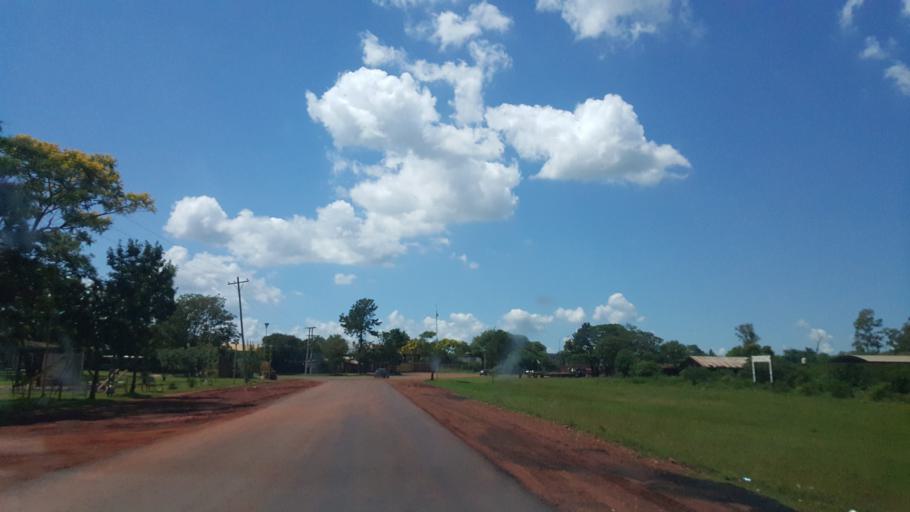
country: AR
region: Corrientes
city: Santo Tome
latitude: -28.5425
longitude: -56.0494
